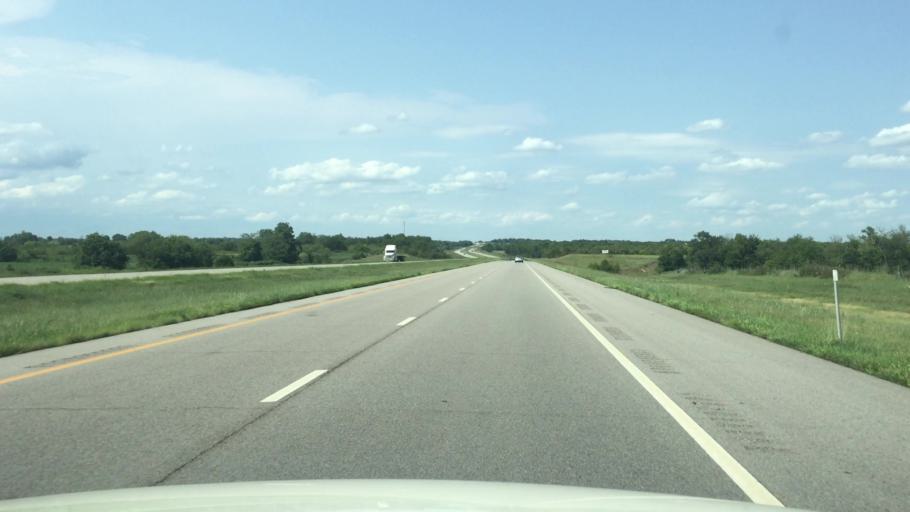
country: US
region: Kansas
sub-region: Linn County
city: La Cygne
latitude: 38.4425
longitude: -94.6862
